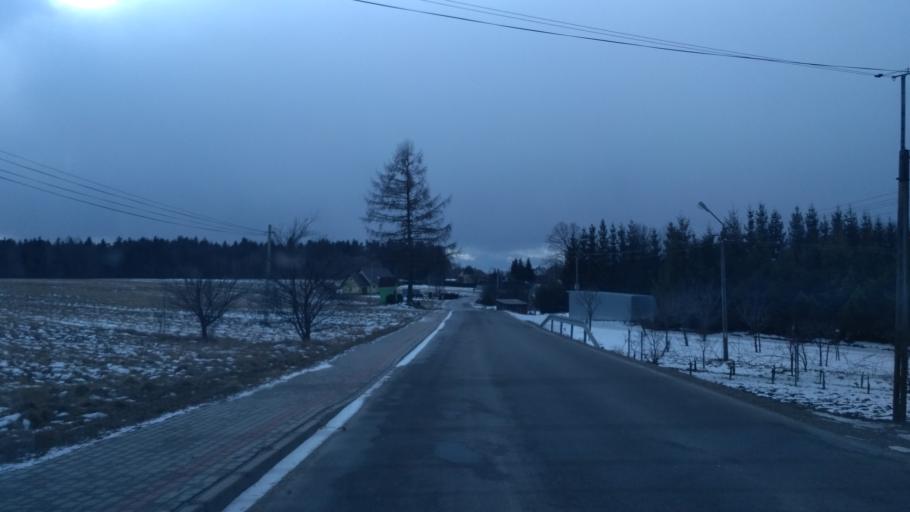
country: PL
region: Subcarpathian Voivodeship
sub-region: Powiat brzozowski
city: Wesola
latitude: 49.8406
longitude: 22.0899
